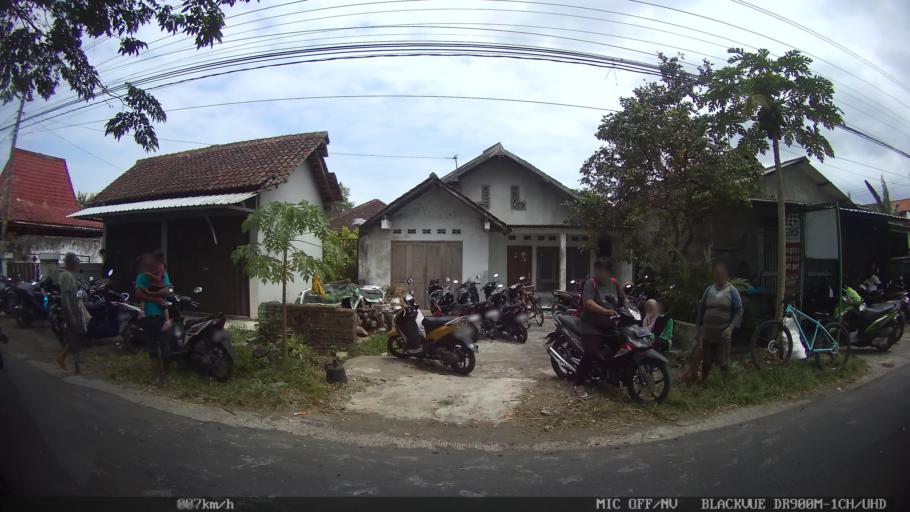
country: ID
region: Daerah Istimewa Yogyakarta
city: Depok
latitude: -7.8089
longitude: 110.4432
